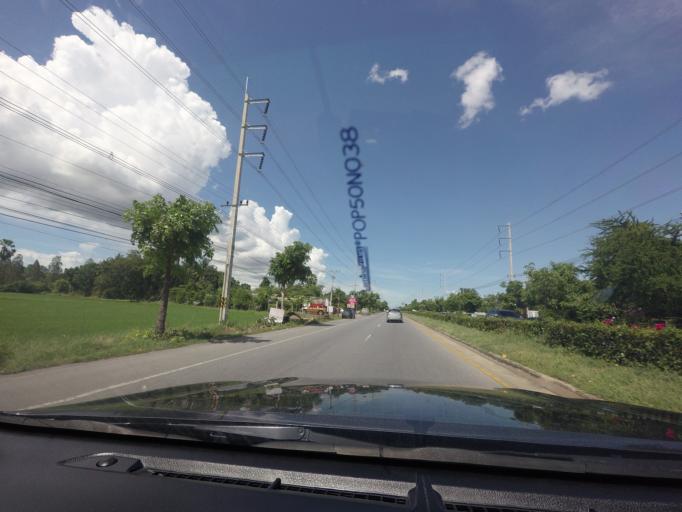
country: TH
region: Kanchanaburi
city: Phanom Thuan
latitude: 14.0681
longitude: 99.6434
